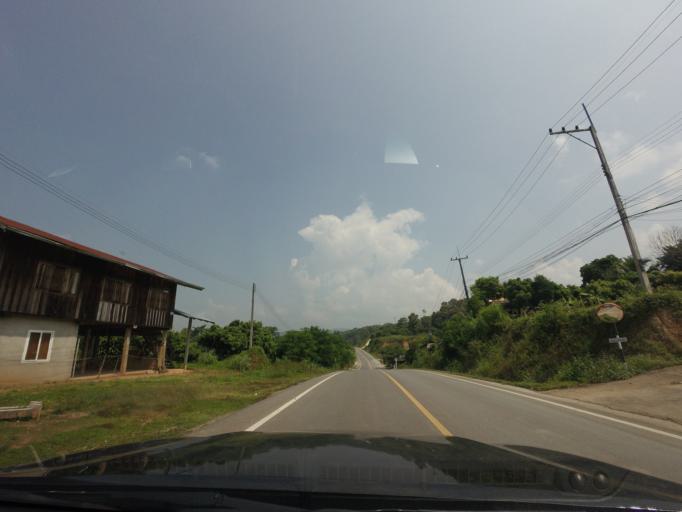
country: TH
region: Nan
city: Nan
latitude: 18.8706
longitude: 100.8319
